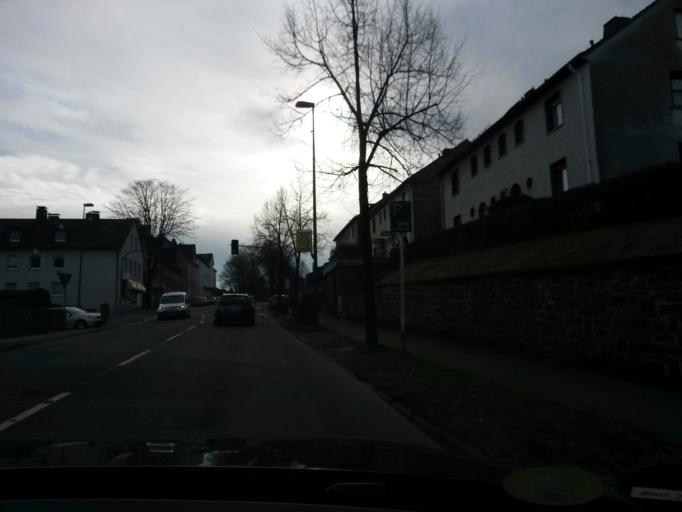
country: DE
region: North Rhine-Westphalia
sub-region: Regierungsbezirk Arnsberg
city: Luedenscheid
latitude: 51.2098
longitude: 7.6493
